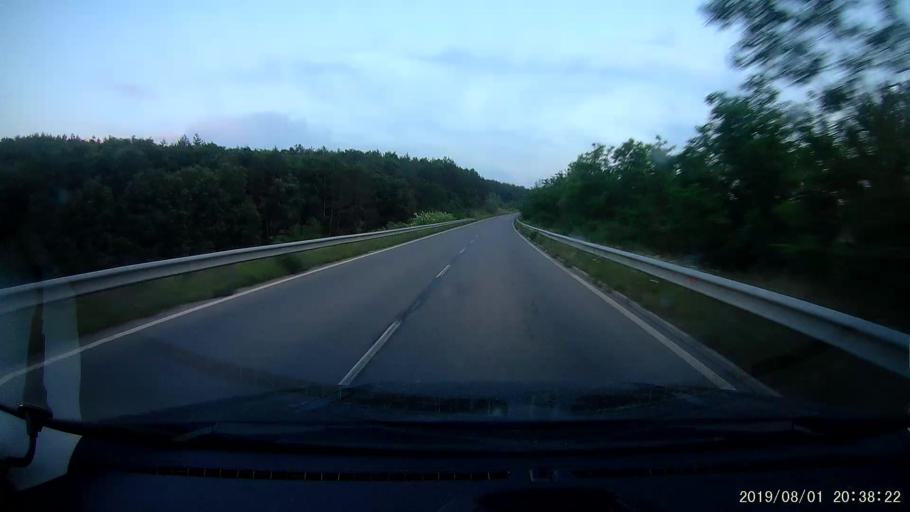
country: BG
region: Yambol
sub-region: Obshtina Elkhovo
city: Elkhovo
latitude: 42.0278
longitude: 26.6009
